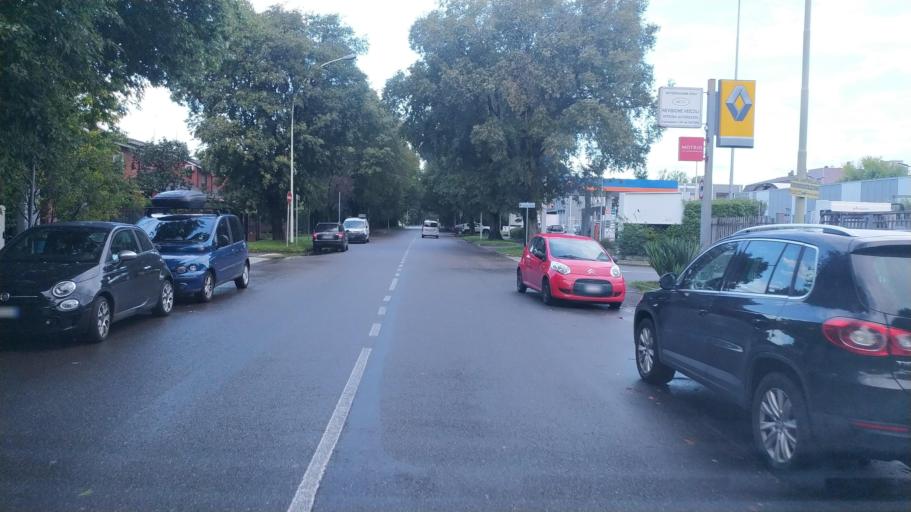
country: IT
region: Lombardy
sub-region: Citta metropolitana di Milano
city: Trezzano sul Naviglio
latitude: 45.4289
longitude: 9.0669
